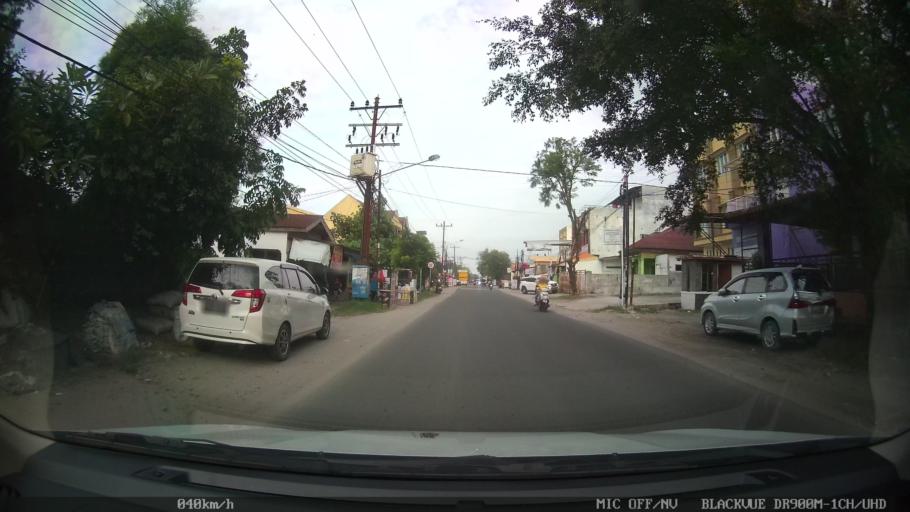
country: ID
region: North Sumatra
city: Sunggal
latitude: 3.5630
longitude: 98.6173
